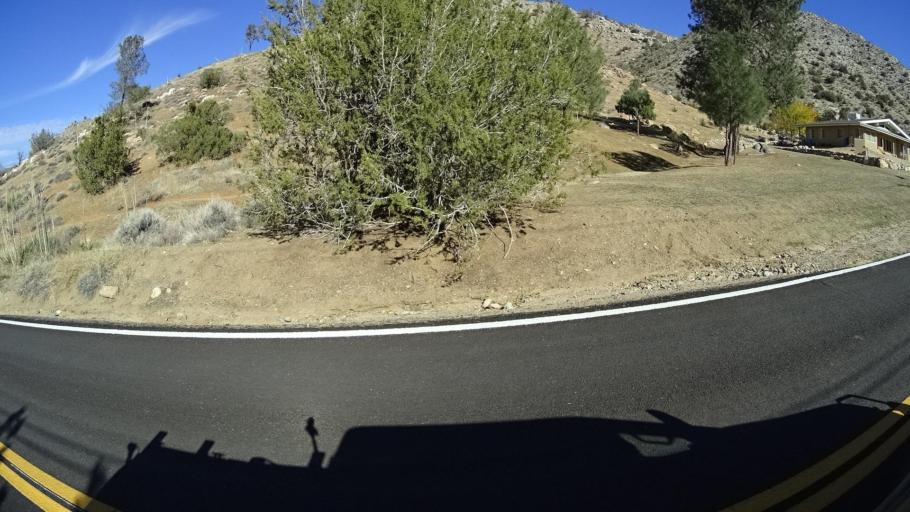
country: US
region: California
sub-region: Kern County
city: Lake Isabella
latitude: 35.5975
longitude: -118.4544
